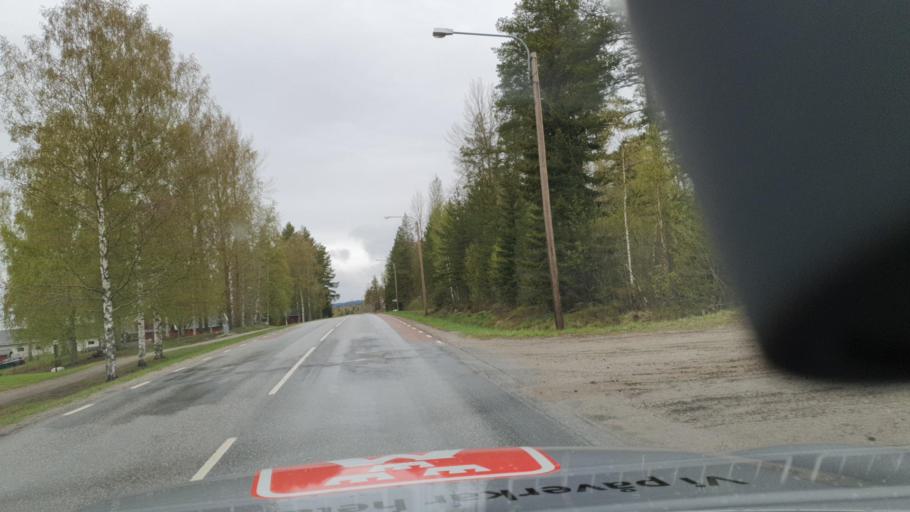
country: SE
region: Vaesternorrland
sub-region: OErnskoeldsviks Kommun
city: Bjasta
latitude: 63.3830
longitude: 18.4721
